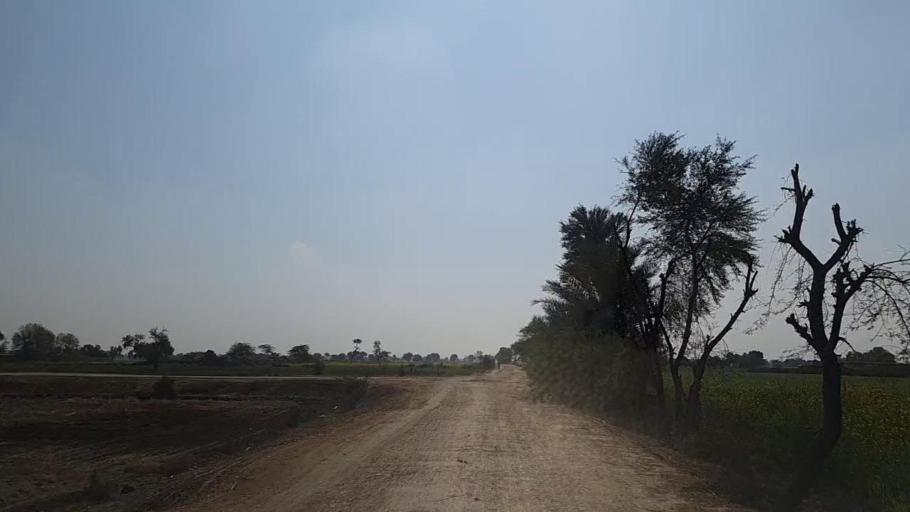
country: PK
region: Sindh
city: Daur
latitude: 26.4557
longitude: 68.2631
